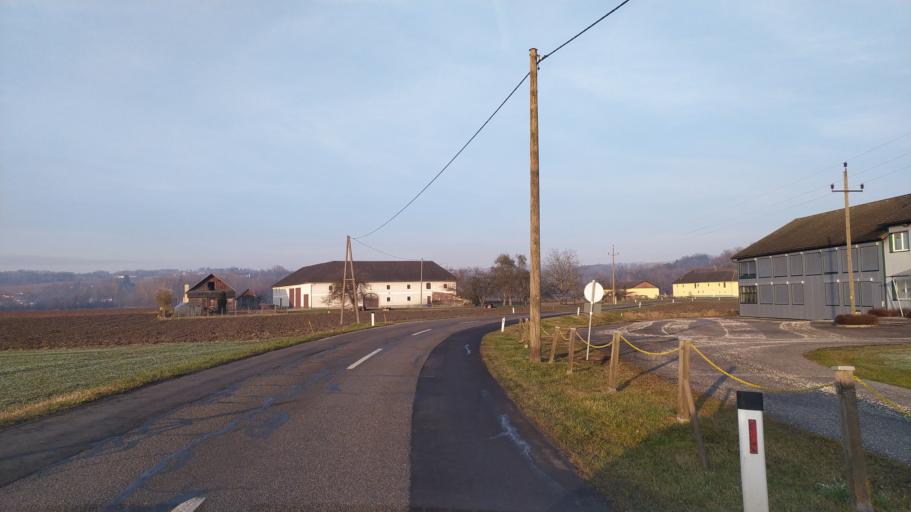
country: AT
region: Upper Austria
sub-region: Politischer Bezirk Urfahr-Umgebung
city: Goldworth
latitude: 48.3337
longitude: 14.1104
